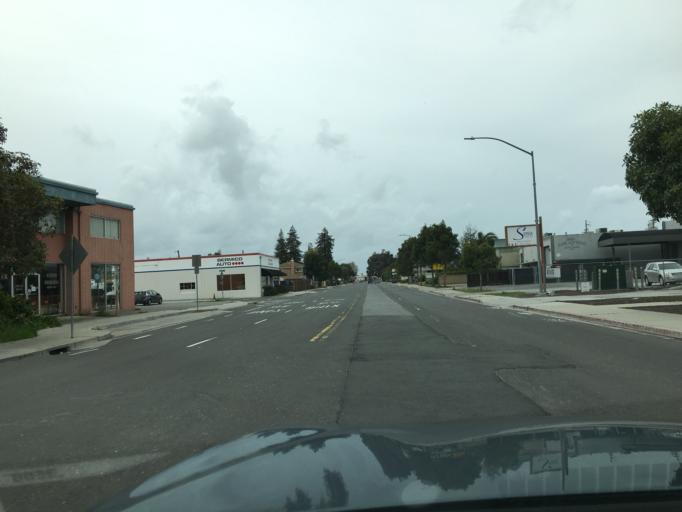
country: US
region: California
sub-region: San Mateo County
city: San Carlos
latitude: 37.5083
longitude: -122.2526
